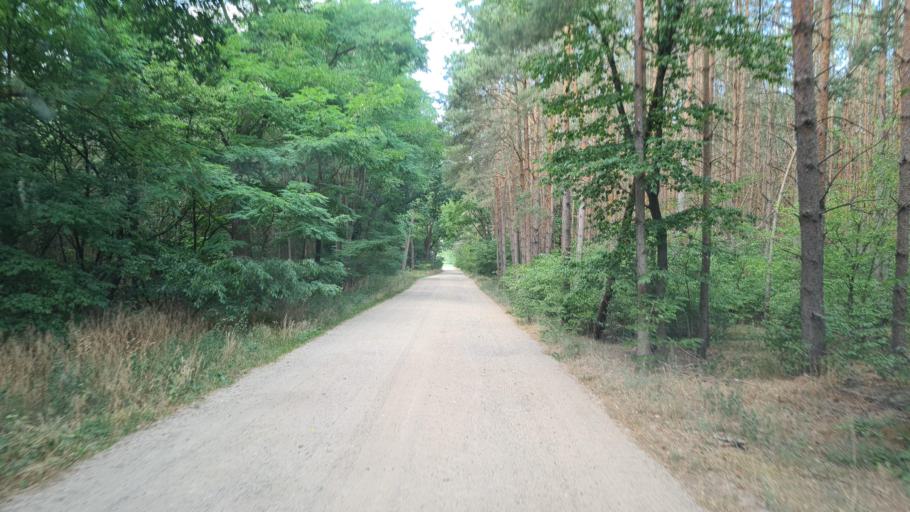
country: DE
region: Brandenburg
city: Golzow
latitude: 52.3226
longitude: 12.5513
